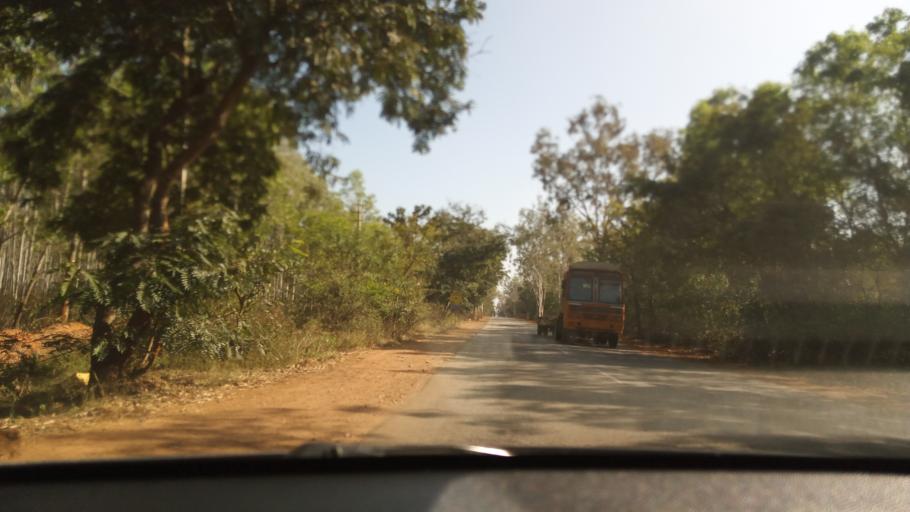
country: IN
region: Karnataka
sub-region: Bangalore Rural
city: Devanhalli
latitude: 13.2692
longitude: 77.7452
